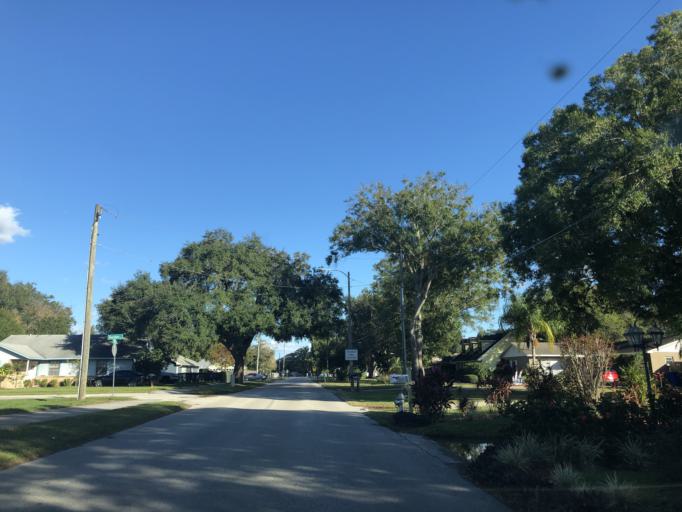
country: US
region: Florida
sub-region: Osceola County
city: Saint Cloud
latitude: 28.2533
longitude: -81.3055
